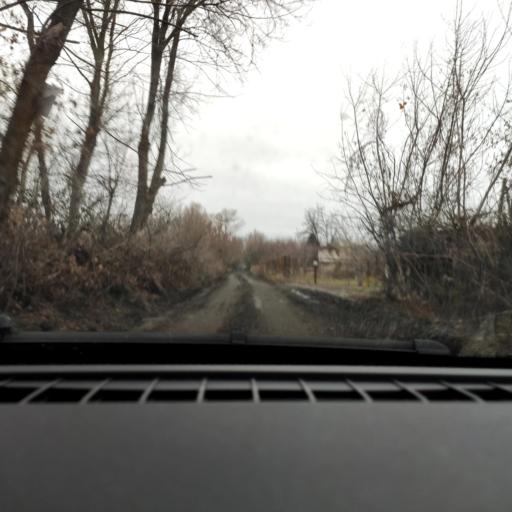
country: RU
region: Voronezj
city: Maslovka
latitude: 51.6074
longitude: 39.2717
